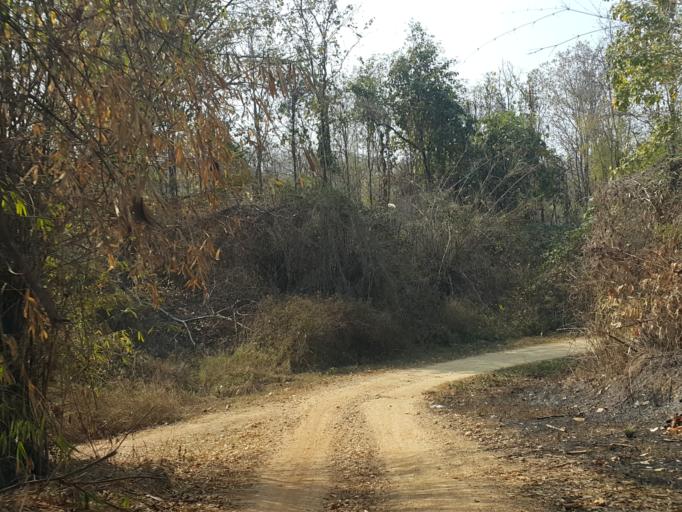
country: TH
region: Chiang Mai
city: Hang Dong
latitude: 18.7186
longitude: 98.8567
